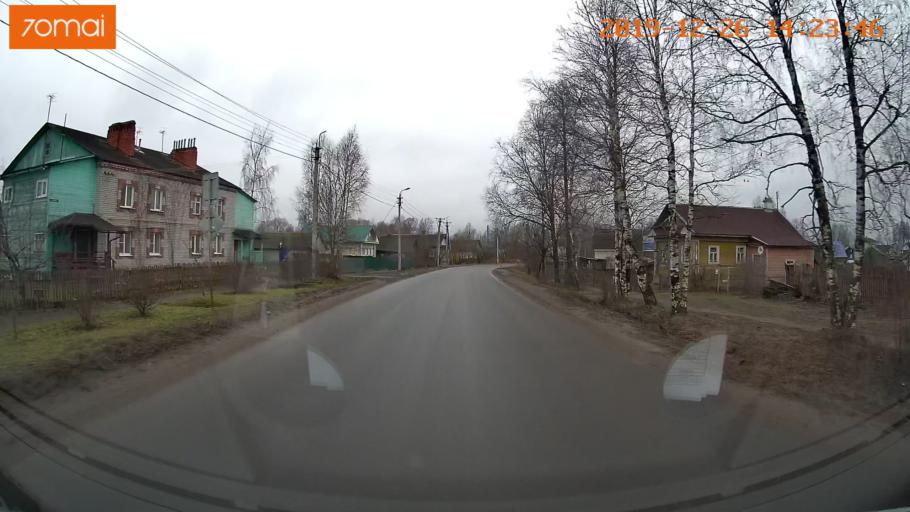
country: RU
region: Jaroslavl
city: Poshekhon'ye
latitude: 58.4980
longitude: 39.1133
